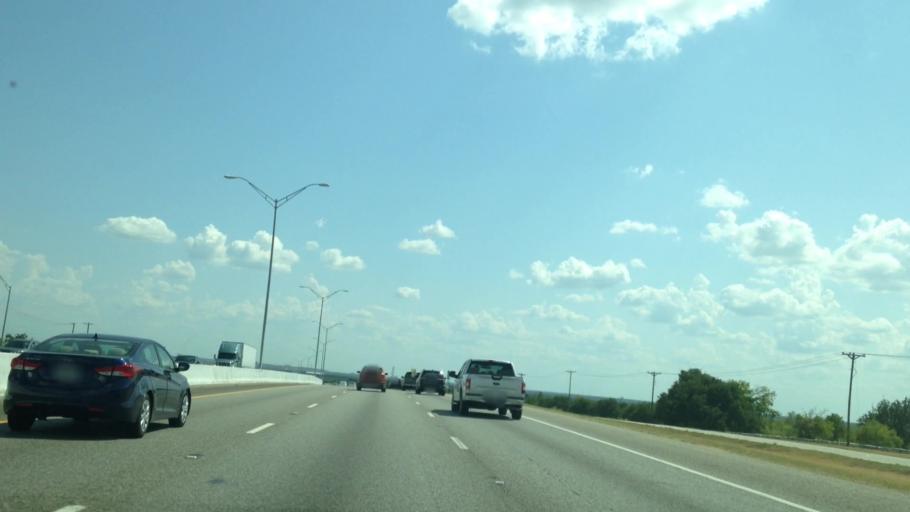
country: US
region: Texas
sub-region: Williamson County
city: Georgetown
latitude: 30.5882
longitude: -97.6926
